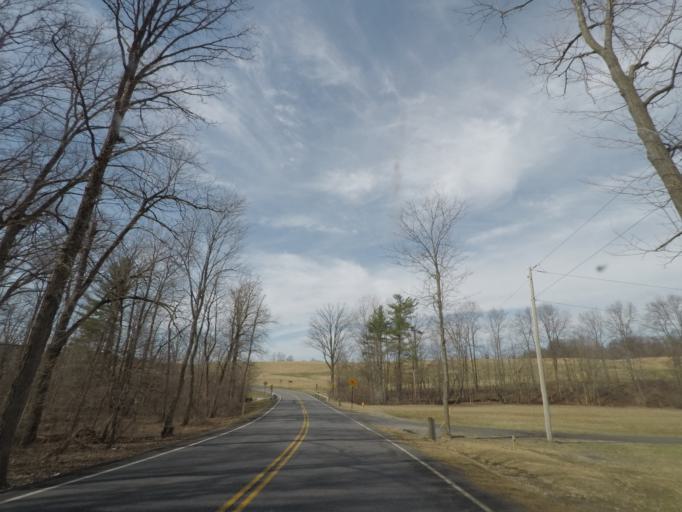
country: US
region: New York
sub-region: Saratoga County
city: Mechanicville
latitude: 42.9048
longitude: -73.7351
